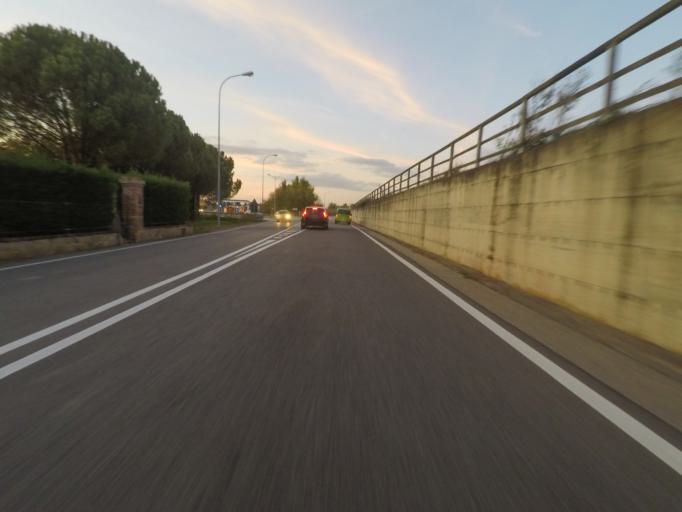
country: IT
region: Tuscany
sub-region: Provincia di Siena
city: Sinalunga
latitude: 43.2102
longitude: 11.7620
